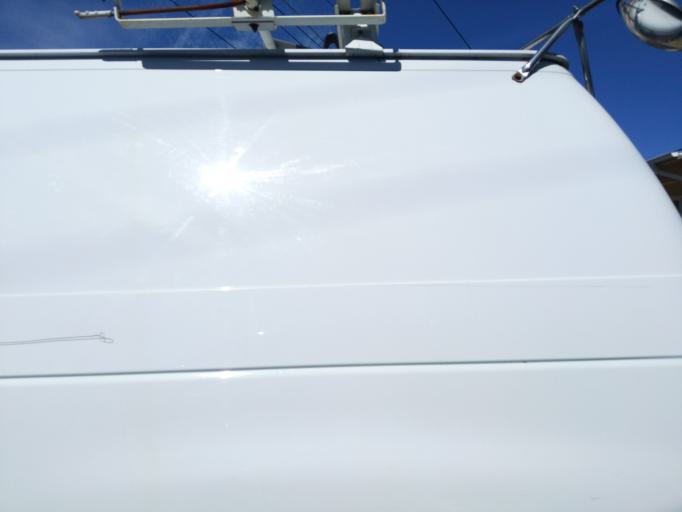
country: US
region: California
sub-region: Alameda County
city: San Leandro
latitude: 37.7692
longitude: -122.1836
